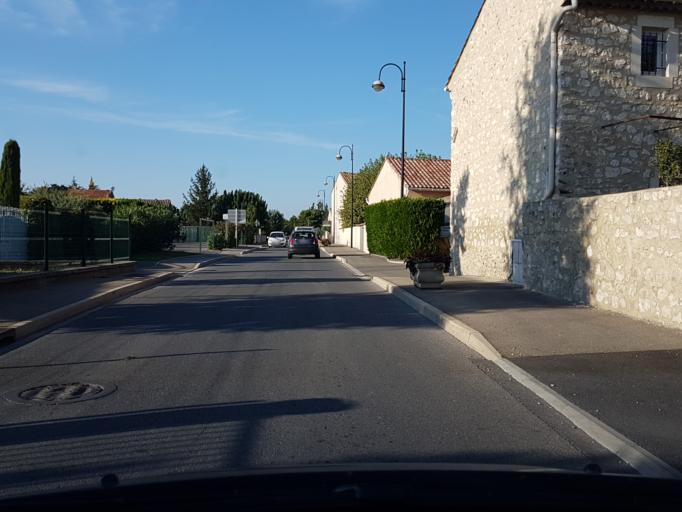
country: FR
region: Provence-Alpes-Cote d'Azur
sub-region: Departement des Bouches-du-Rhone
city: Molleges
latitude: 43.8082
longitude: 4.9490
